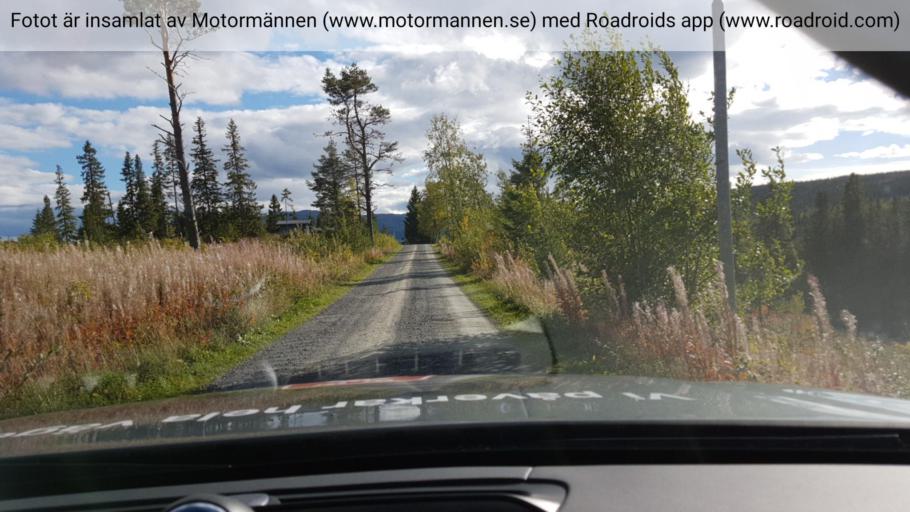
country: SE
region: Jaemtland
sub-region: Are Kommun
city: Jarpen
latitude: 63.2326
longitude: 13.6777
